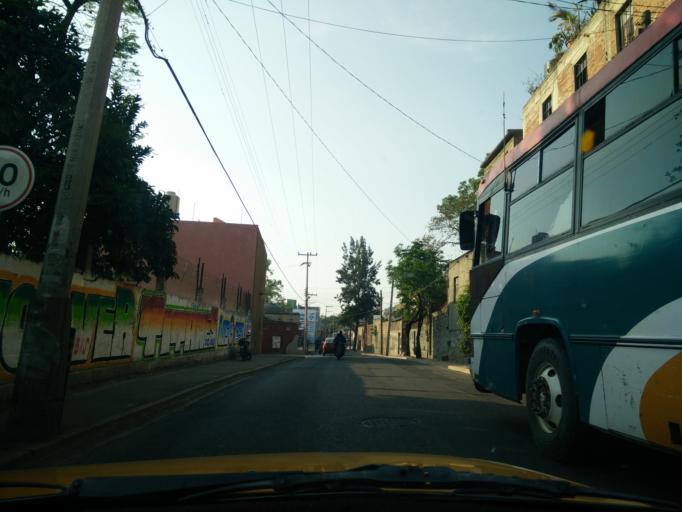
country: MX
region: Oaxaca
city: Oaxaca de Juarez
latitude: 17.0692
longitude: -96.7360
